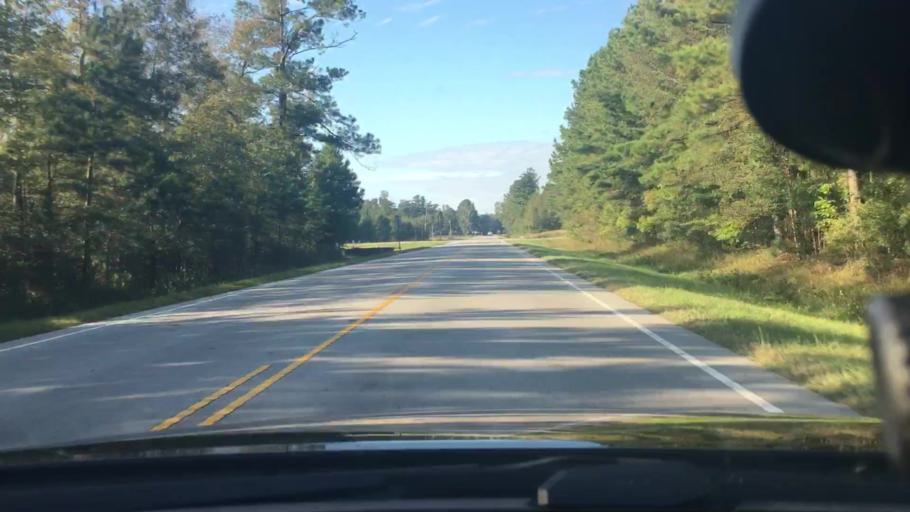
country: US
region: North Carolina
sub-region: Craven County
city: Vanceboro
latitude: 35.3258
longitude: -77.1476
